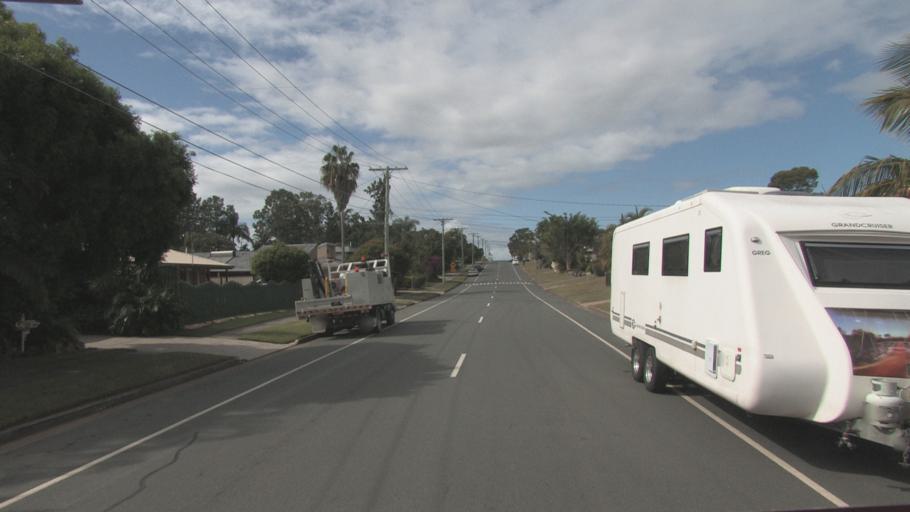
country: AU
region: Queensland
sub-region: Brisbane
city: Sunnybank Hills
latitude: -27.6651
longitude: 153.0369
